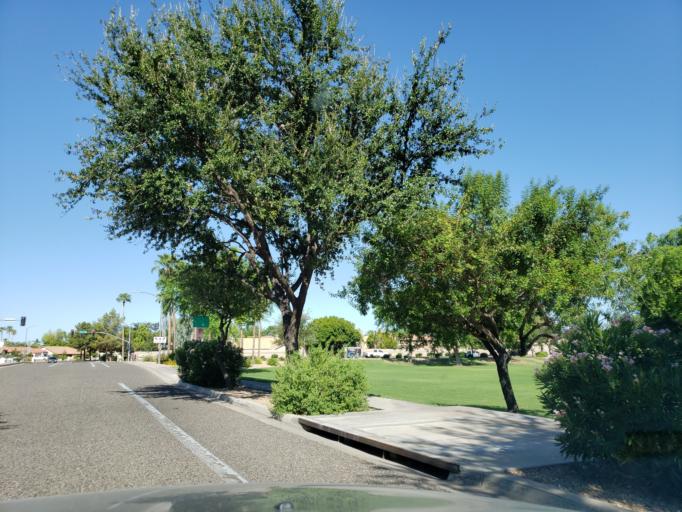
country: US
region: Arizona
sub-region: Maricopa County
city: Peoria
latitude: 33.6603
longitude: -112.2018
